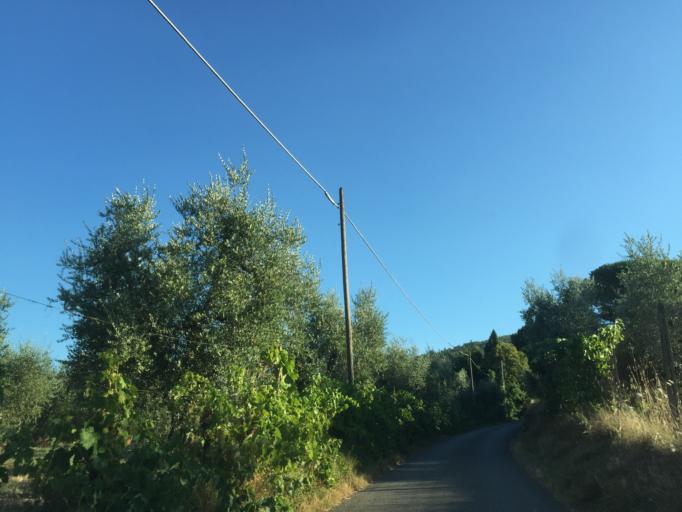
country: IT
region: Tuscany
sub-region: Provincia di Pistoia
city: Pistoia
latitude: 43.9449
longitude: 10.9522
